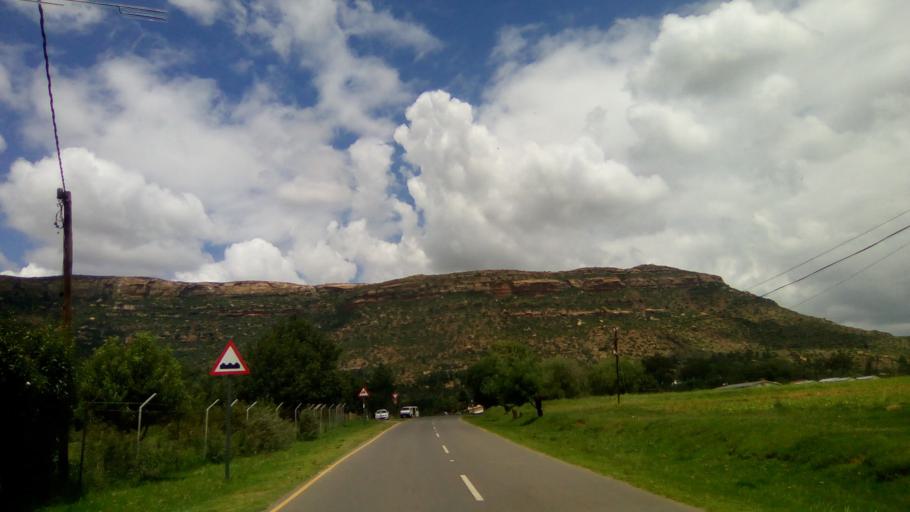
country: LS
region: Maseru
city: Nako
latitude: -29.6250
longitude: 27.5034
